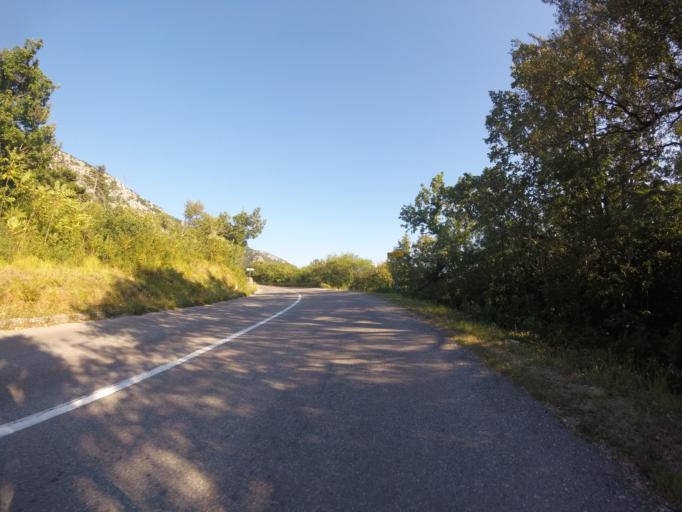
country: HR
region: Primorsko-Goranska
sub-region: Grad Crikvenica
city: Crikvenica
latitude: 45.2124
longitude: 14.7077
